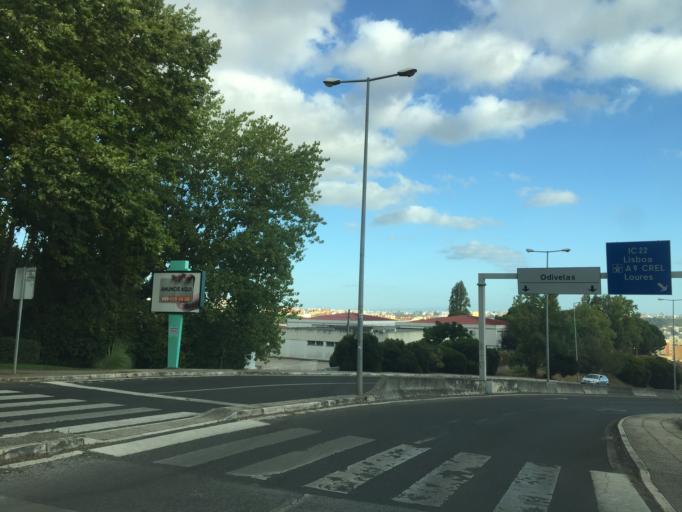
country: PT
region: Lisbon
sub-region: Odivelas
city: Ramada
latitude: 38.8040
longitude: -9.1864
